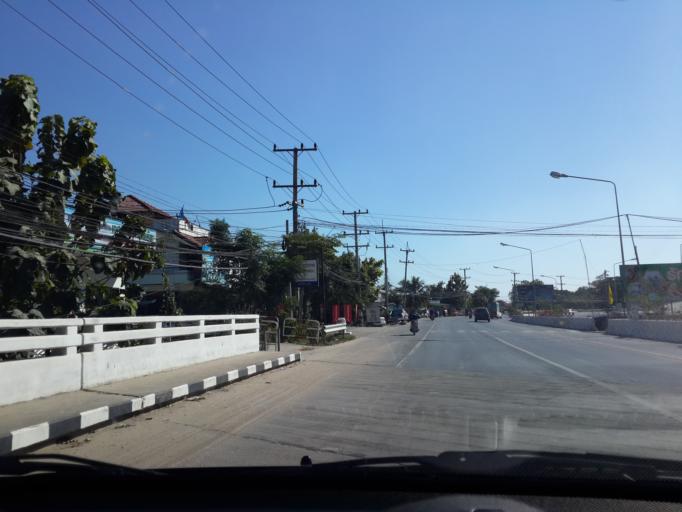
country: TH
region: Chiang Mai
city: Chiang Mai
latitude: 18.7458
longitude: 98.9417
